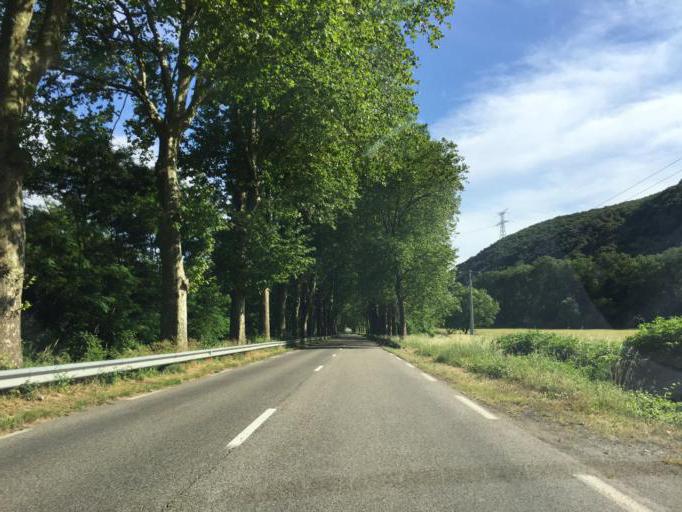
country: FR
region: Rhone-Alpes
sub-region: Departement de la Drome
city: Saulce-sur-Rhone
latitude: 44.6887
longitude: 4.7722
